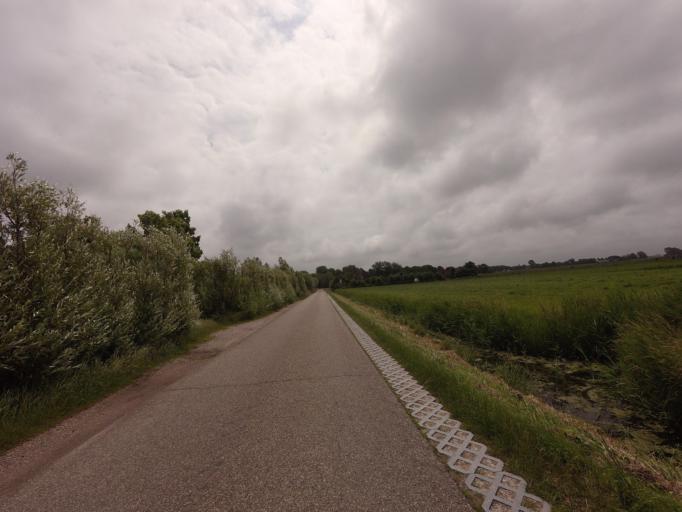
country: NL
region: North Holland
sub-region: Gemeente Schagen
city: Schagen
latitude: 52.7855
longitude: 4.7740
